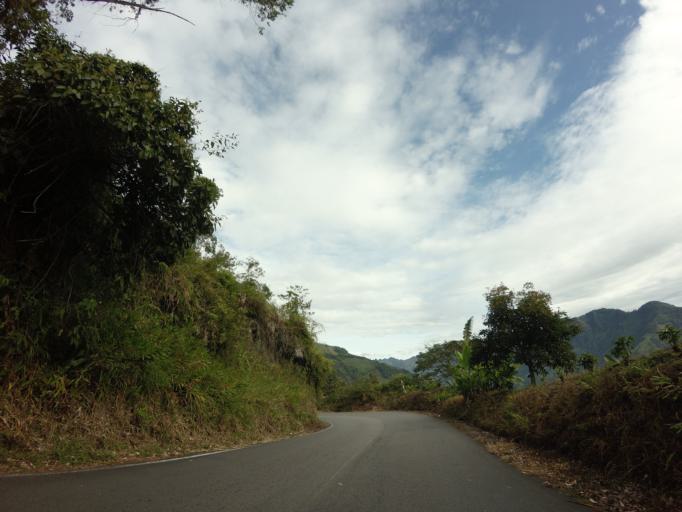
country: CO
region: Tolima
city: Casabianca
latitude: 5.1421
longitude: -75.1307
